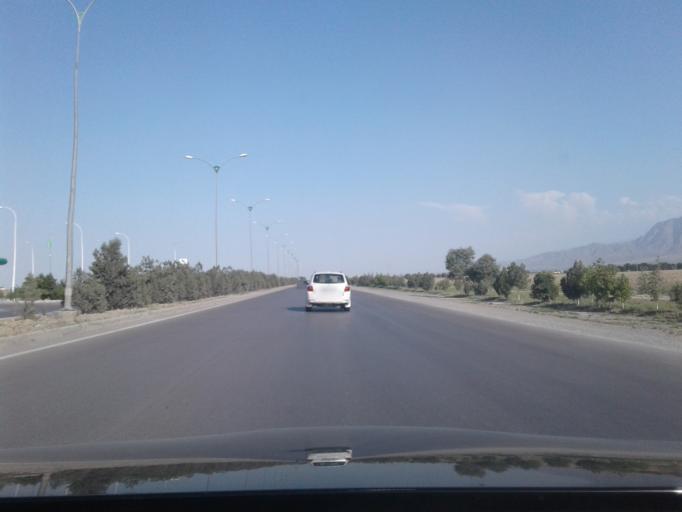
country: TM
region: Ahal
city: Abadan
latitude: 38.1402
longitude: 58.0004
